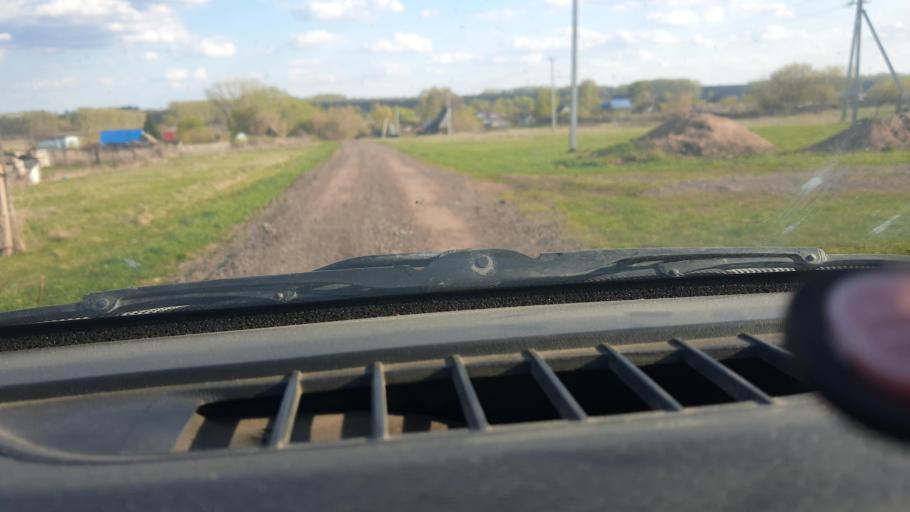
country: RU
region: Bashkortostan
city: Chishmy
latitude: 54.5969
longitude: 55.2703
